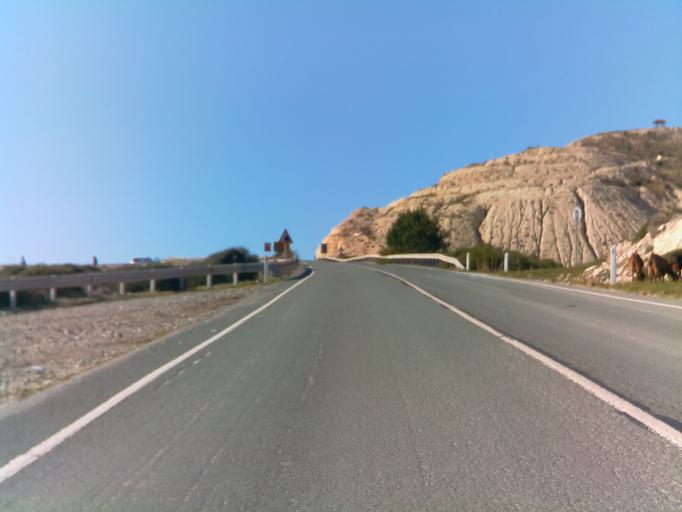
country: CY
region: Limassol
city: Pissouri
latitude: 34.6603
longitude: 32.6436
